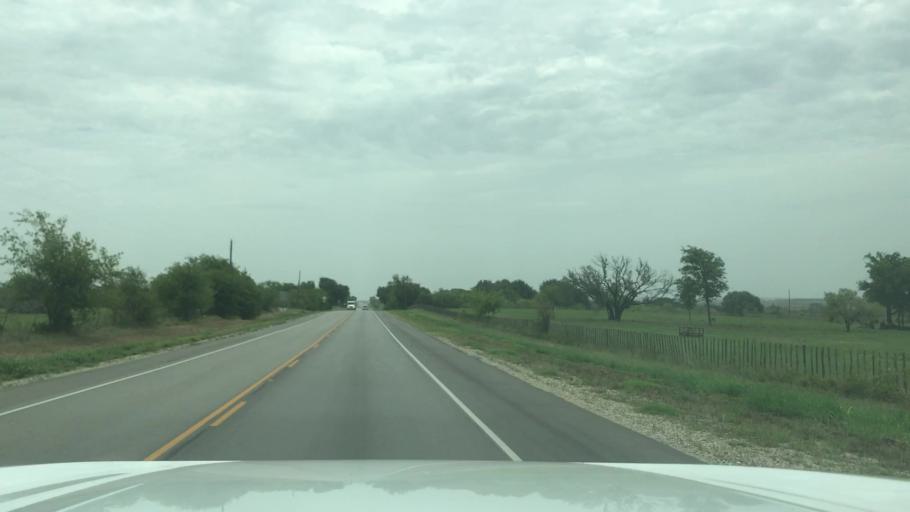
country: US
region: Texas
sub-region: Erath County
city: Dublin
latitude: 32.0855
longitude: -98.2537
